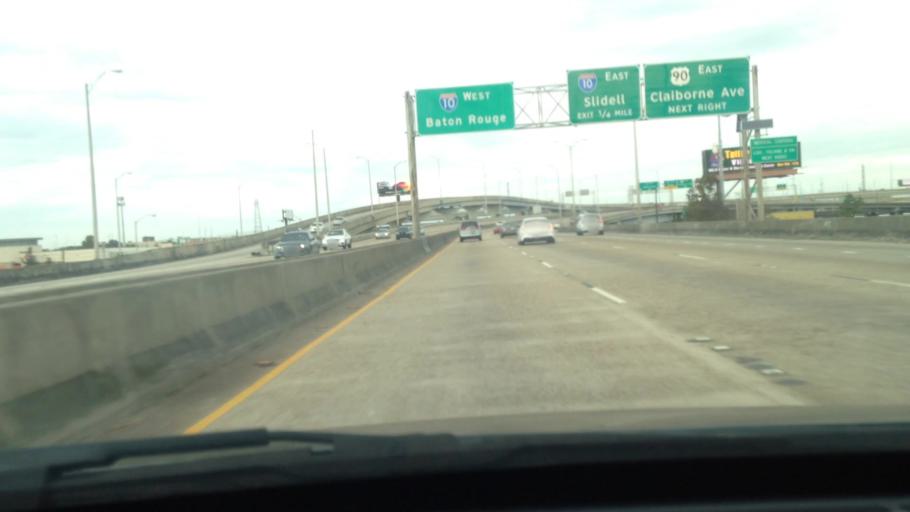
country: US
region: Louisiana
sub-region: Orleans Parish
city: New Orleans
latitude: 29.9475
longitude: -90.0824
